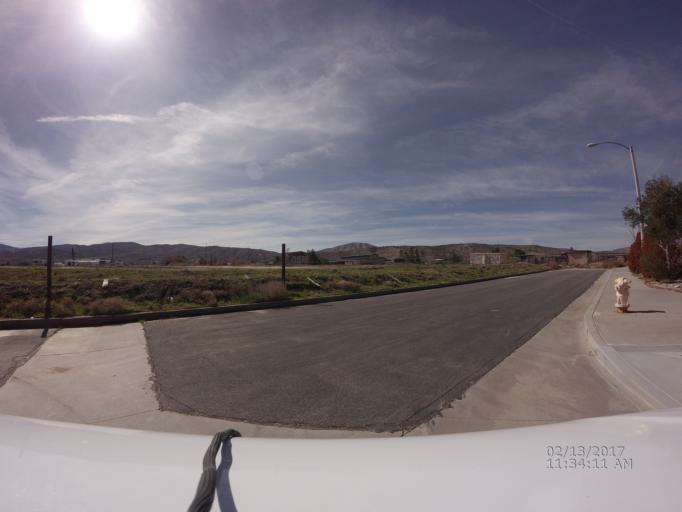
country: US
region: California
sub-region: Los Angeles County
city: Littlerock
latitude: 34.5230
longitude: -118.0009
